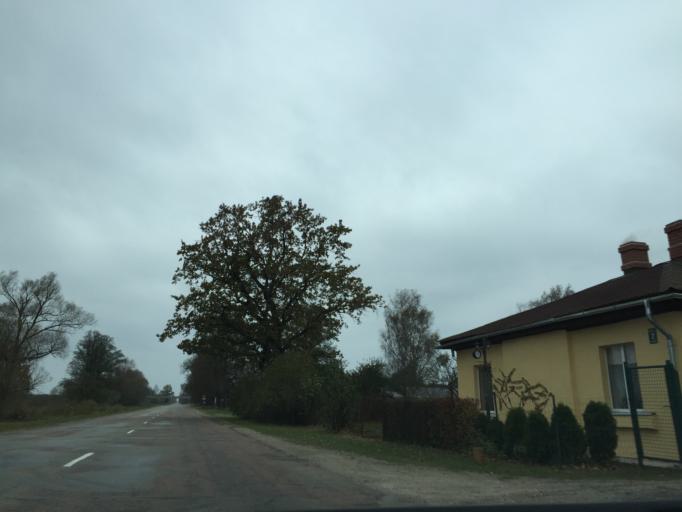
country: LV
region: Marupe
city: Marupe
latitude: 56.8411
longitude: 24.0408
